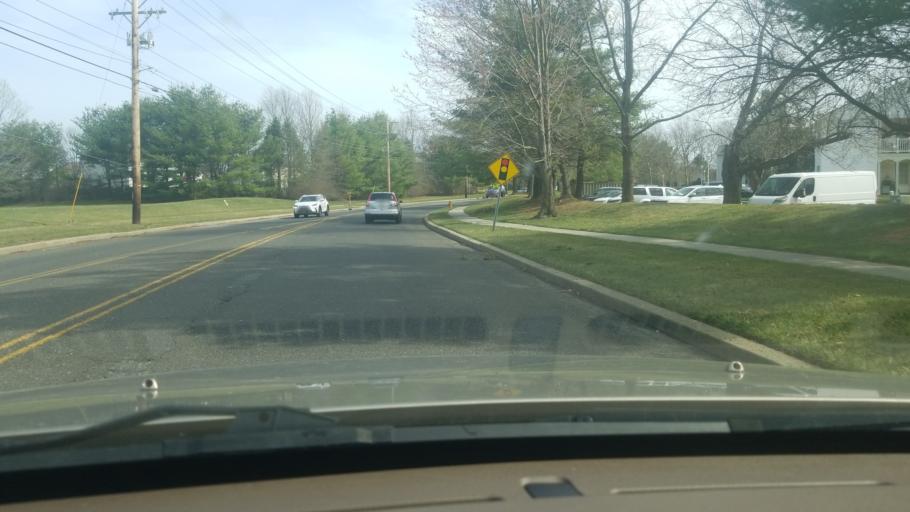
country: US
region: New Jersey
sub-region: Monmouth County
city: West Freehold
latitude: 40.2475
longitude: -74.3077
